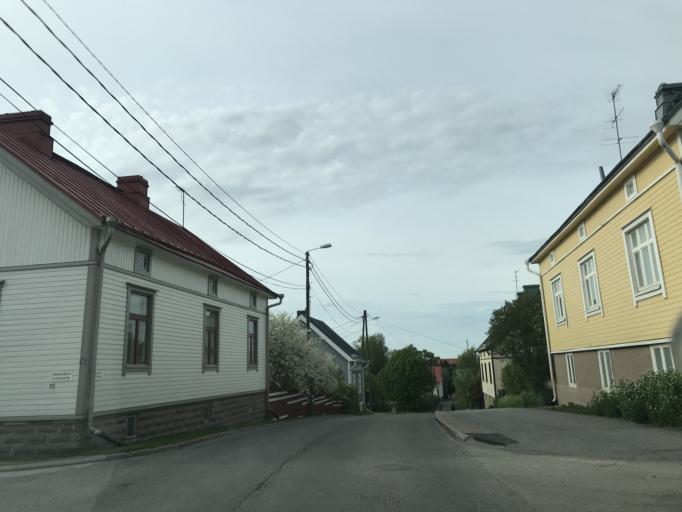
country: FI
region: Varsinais-Suomi
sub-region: Turku
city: Turku
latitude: 60.4534
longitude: 22.3079
